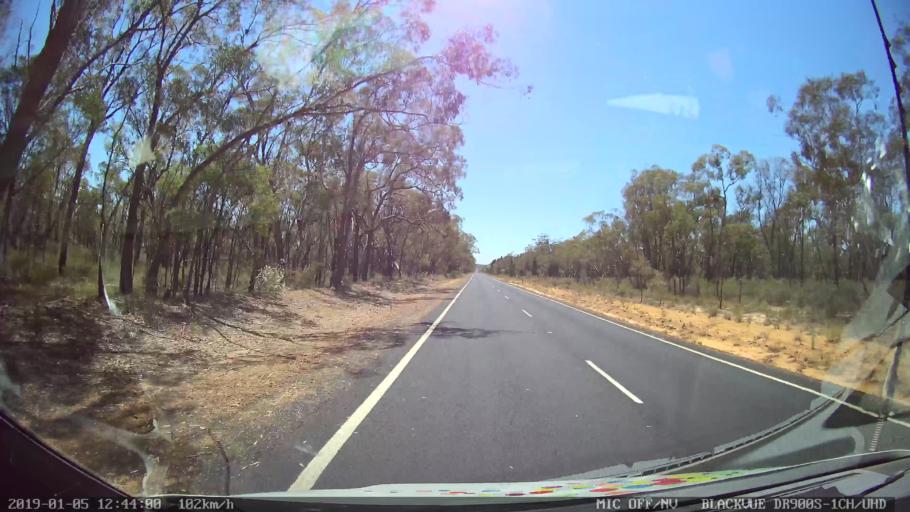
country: AU
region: New South Wales
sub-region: Warrumbungle Shire
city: Coonabarabran
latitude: -31.1422
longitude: 149.5316
